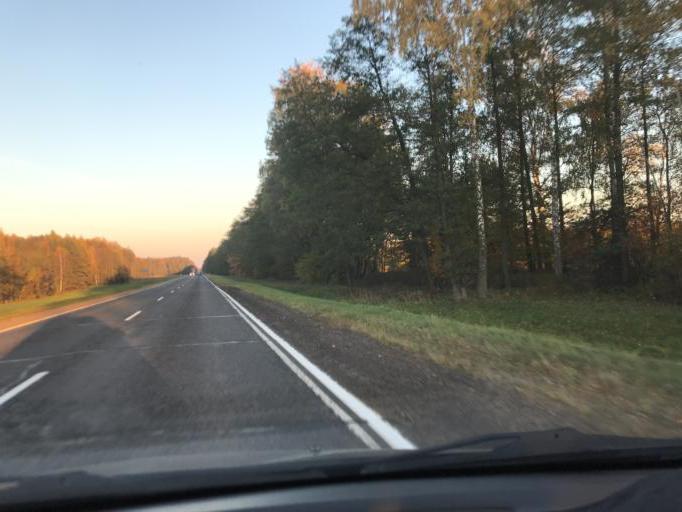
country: BY
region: Mogilev
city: Hlusk
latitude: 53.0689
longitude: 28.5799
